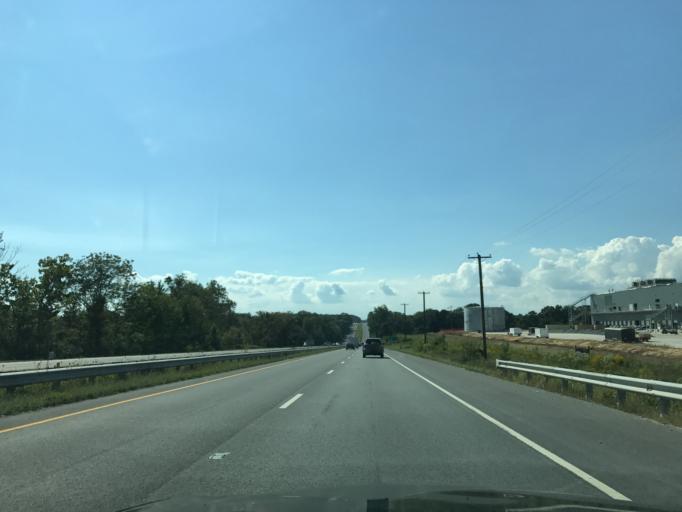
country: US
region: Maryland
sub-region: Cecil County
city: Charlestown
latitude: 39.5822
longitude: -76.0242
